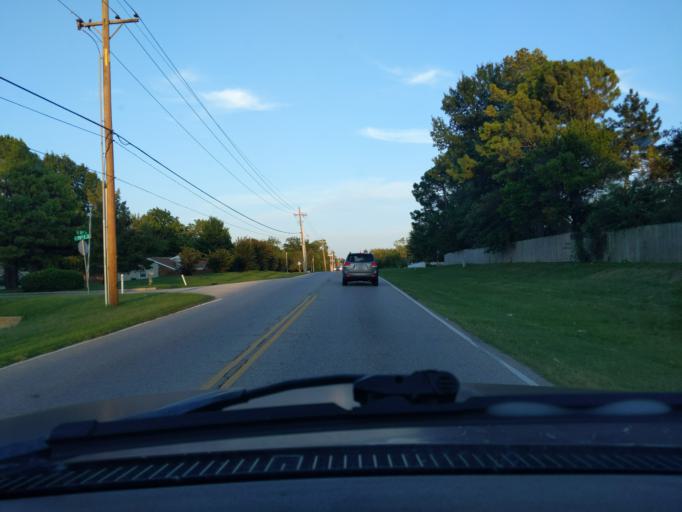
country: US
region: Oklahoma
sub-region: Tulsa County
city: Jenks
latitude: 36.0464
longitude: -95.8929
